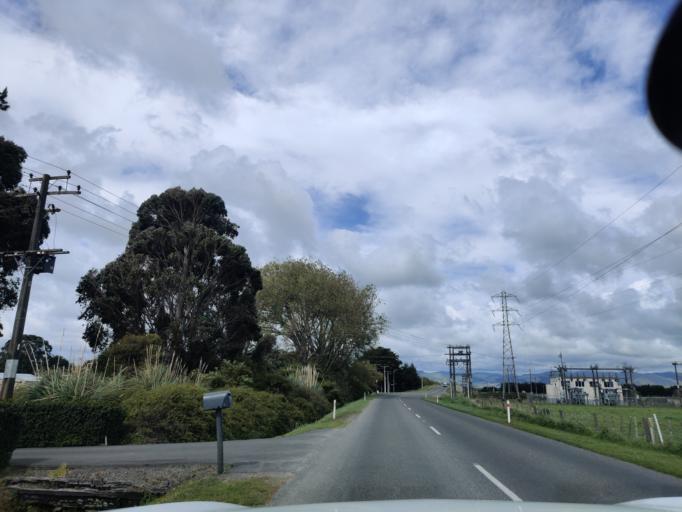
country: NZ
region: Manawatu-Wanganui
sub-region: Palmerston North City
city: Palmerston North
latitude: -40.3641
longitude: 175.5504
